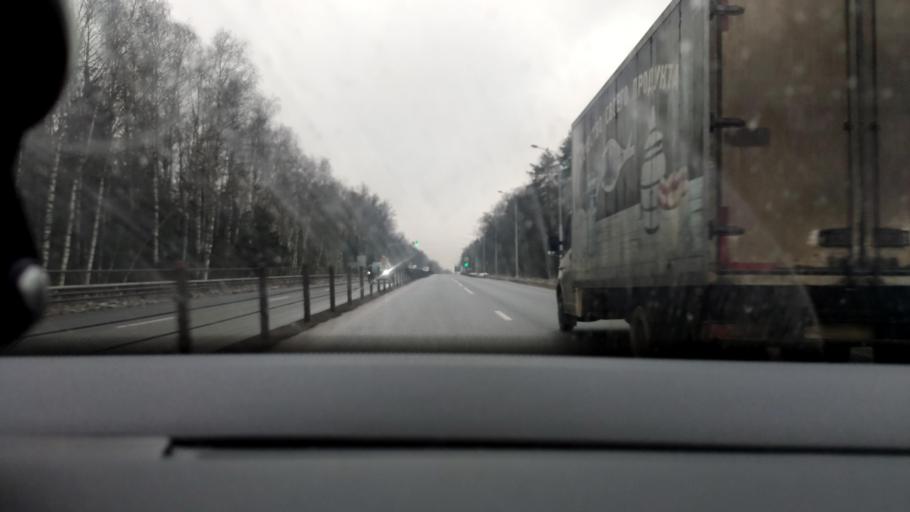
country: RU
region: Moskovskaya
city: Sergiyev Posad
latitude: 56.2449
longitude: 38.1192
